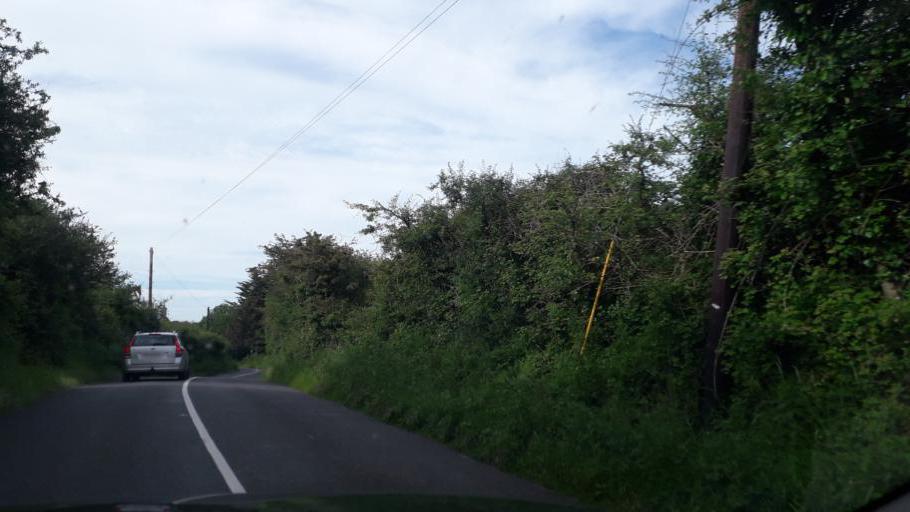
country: IE
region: Leinster
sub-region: Loch Garman
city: Courtown
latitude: 52.5649
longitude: -6.2312
